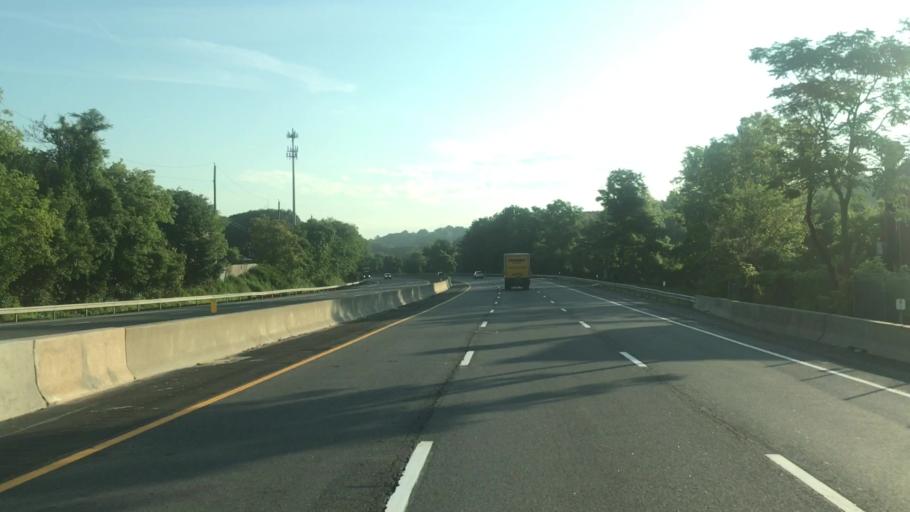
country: US
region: New York
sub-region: Westchester County
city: Ardsley
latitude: 41.0122
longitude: -73.8491
